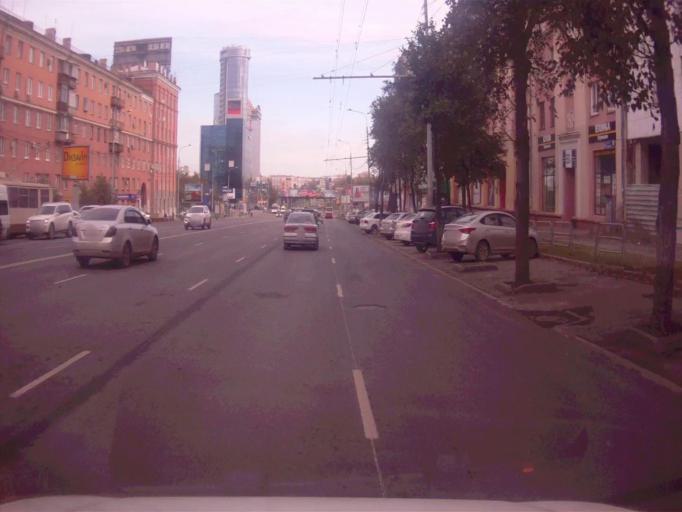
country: RU
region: Chelyabinsk
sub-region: Gorod Chelyabinsk
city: Chelyabinsk
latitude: 55.1608
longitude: 61.4220
